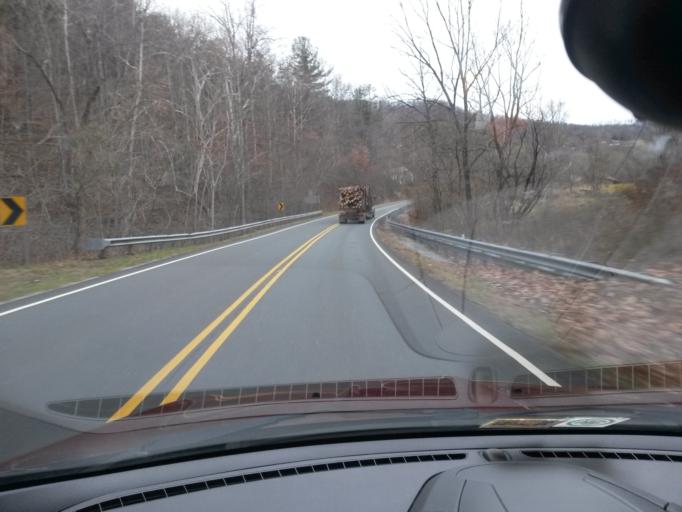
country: US
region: Virginia
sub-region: City of Buena Vista
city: Buena Vista
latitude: 37.6863
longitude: -79.2378
